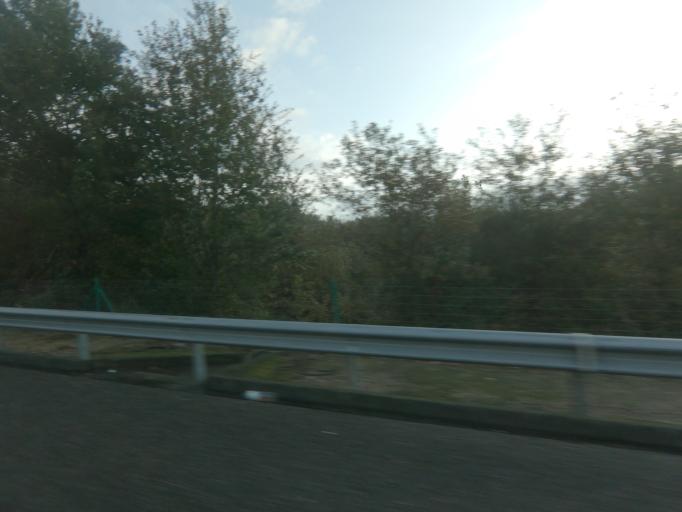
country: ES
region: Galicia
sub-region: Provincia de Pontevedra
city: Porrino
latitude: 42.1088
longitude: -8.6504
